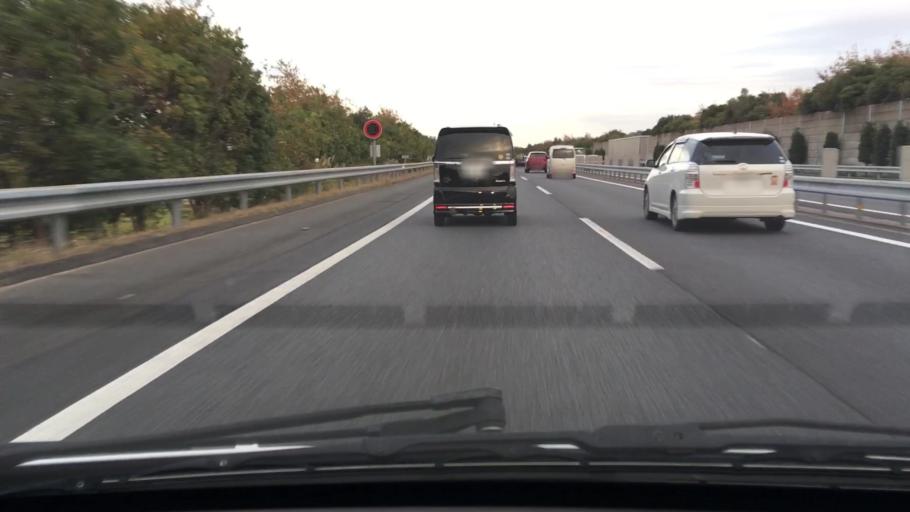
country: JP
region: Chiba
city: Ichihara
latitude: 35.5162
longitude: 140.1181
